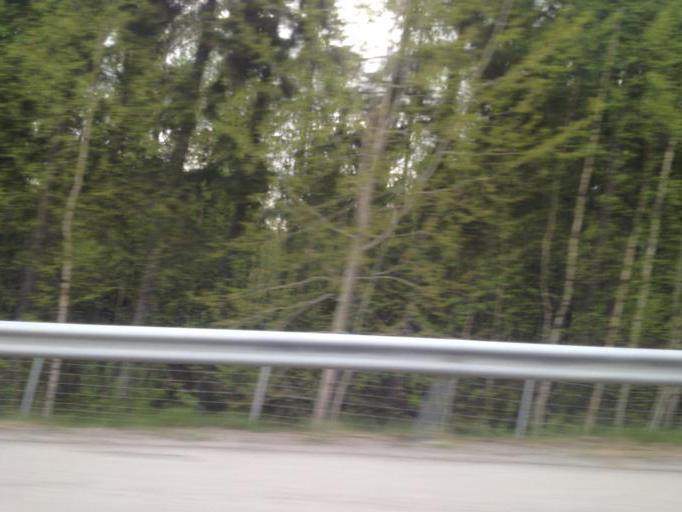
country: FI
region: Haeme
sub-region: Haemeenlinna
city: Haemeenlinna
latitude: 60.9586
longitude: 24.4844
